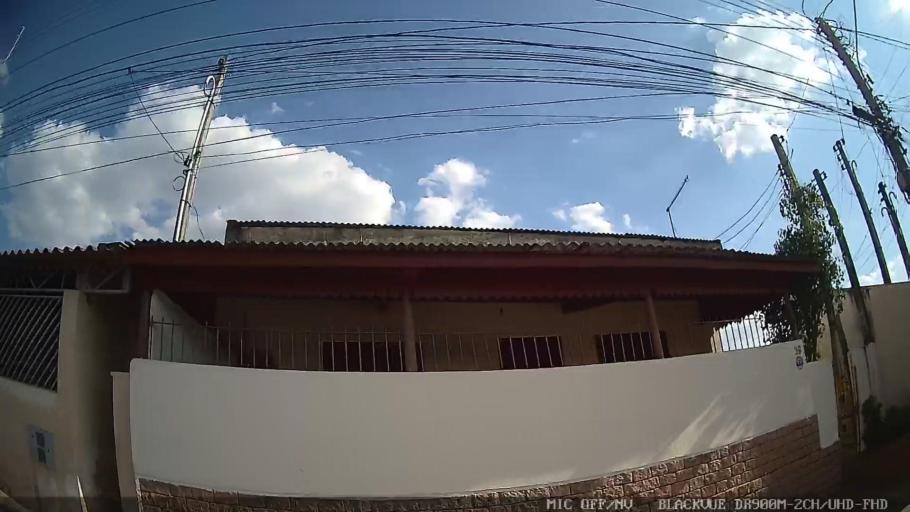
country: BR
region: Sao Paulo
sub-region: Cabreuva
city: Cabreuva
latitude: -23.2550
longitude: -47.0602
